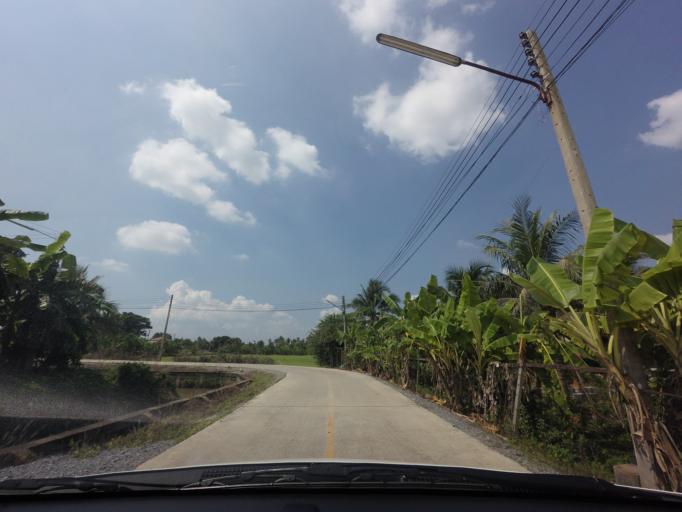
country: TH
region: Nakhon Pathom
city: Nakhon Chai Si
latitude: 13.8112
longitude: 100.1953
